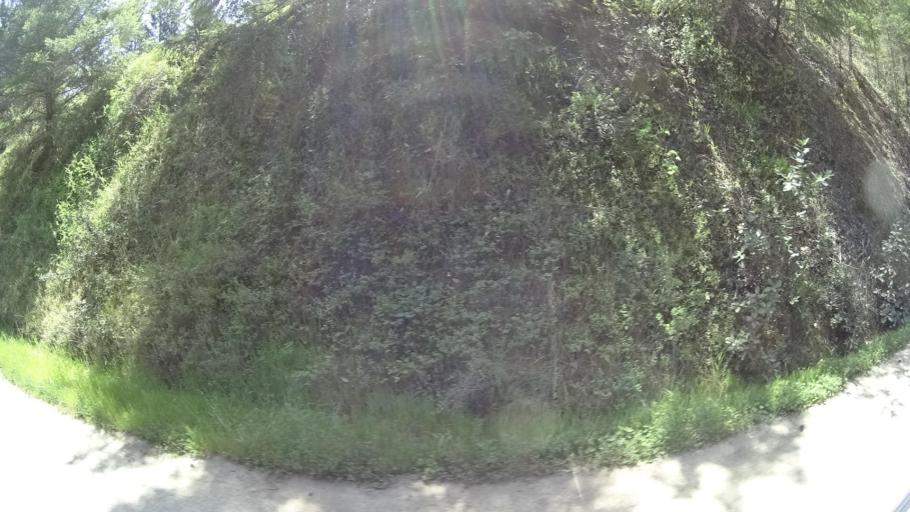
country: US
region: California
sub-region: Humboldt County
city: Redway
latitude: 40.1974
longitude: -123.5257
